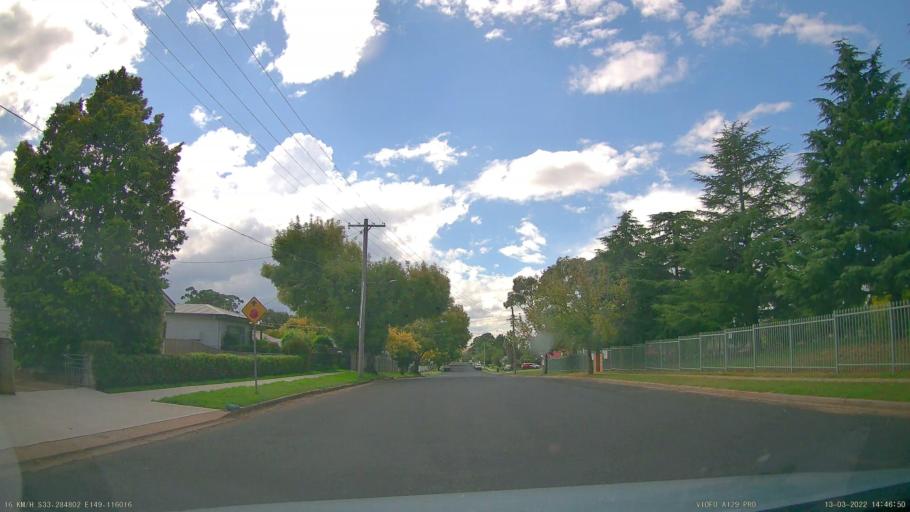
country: AU
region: New South Wales
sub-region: Orange Municipality
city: Orange
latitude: -33.2847
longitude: 149.1160
